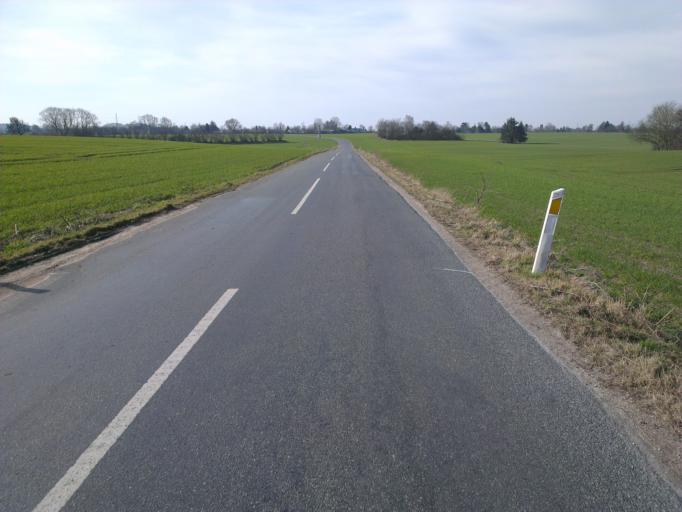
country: DK
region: Capital Region
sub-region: Frederikssund Kommune
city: Jaegerspris
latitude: 55.8180
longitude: 11.9553
